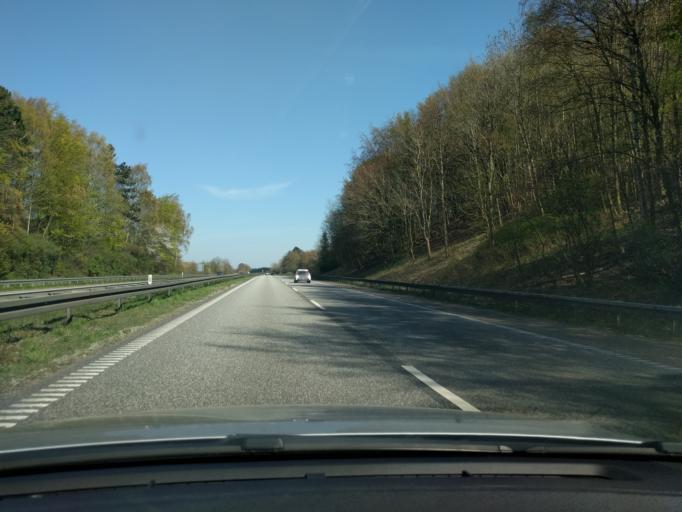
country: DK
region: Zealand
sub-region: Slagelse Kommune
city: Slagelse
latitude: 55.4006
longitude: 11.3886
